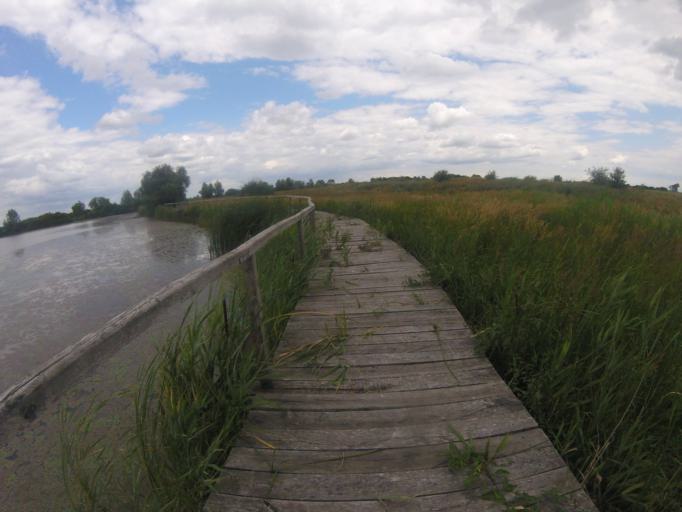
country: HU
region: Hajdu-Bihar
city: Egyek
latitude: 47.5679
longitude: 20.9382
